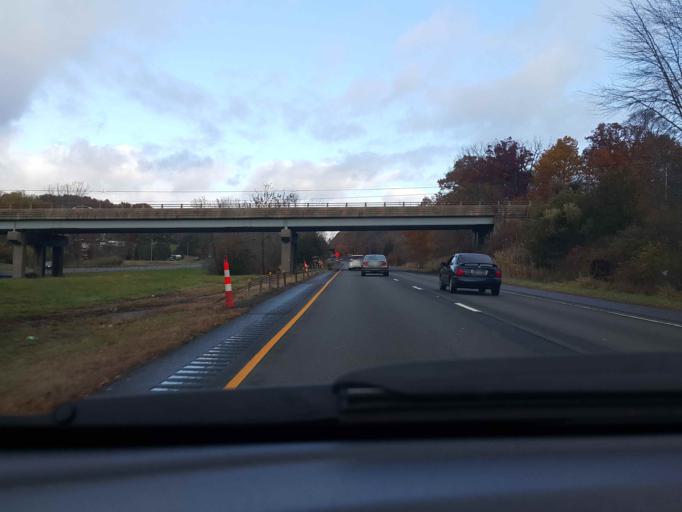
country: US
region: Connecticut
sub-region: Middlesex County
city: Cromwell
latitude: 41.6034
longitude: -72.6732
